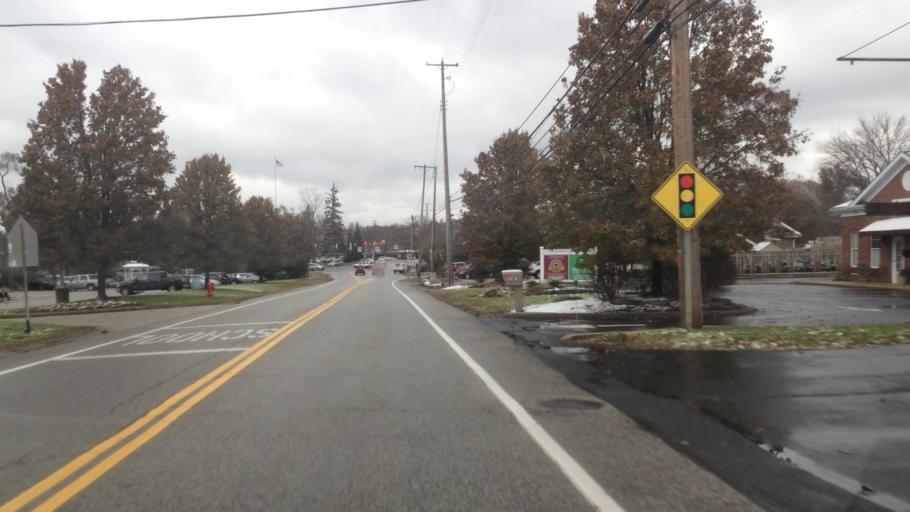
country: US
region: Ohio
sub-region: Summit County
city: Macedonia
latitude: 41.3127
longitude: -81.5375
